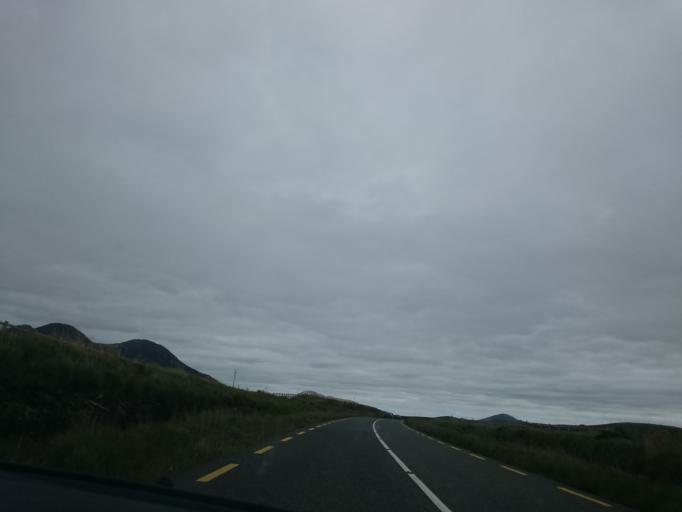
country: IE
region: Connaught
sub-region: County Galway
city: Clifden
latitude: 53.4804
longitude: -9.9191
